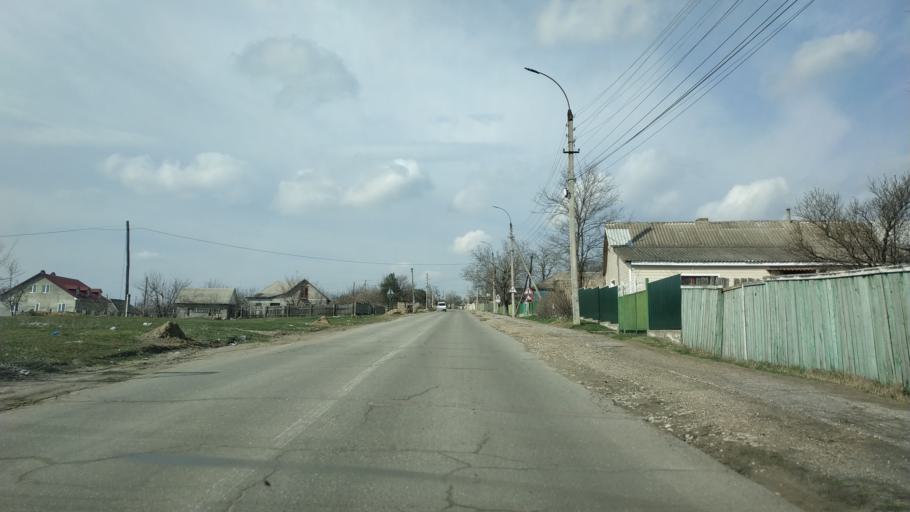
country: MD
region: Gagauzia
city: Vulcanesti
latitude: 45.6893
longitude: 28.4064
